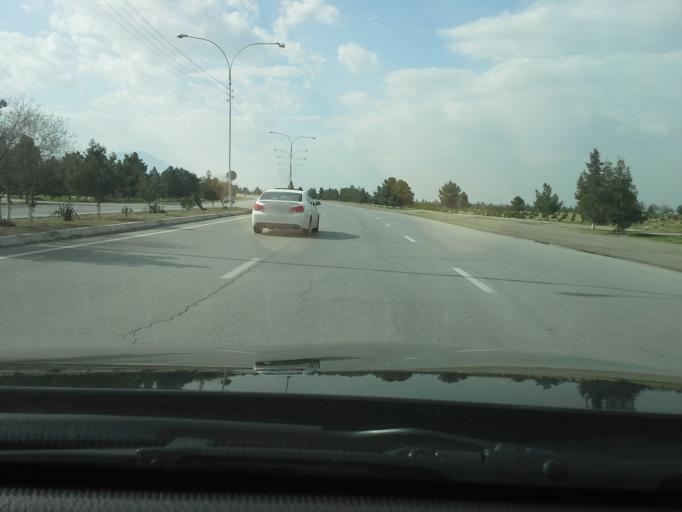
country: TM
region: Ahal
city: Ashgabat
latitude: 37.9692
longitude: 58.2991
